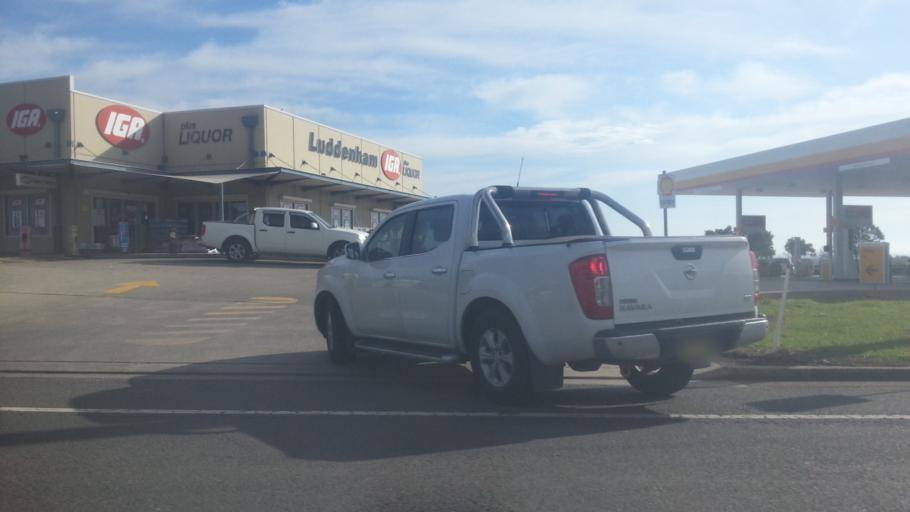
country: AU
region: New South Wales
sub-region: Liverpool
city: Luddenham
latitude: -33.8843
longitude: 150.6938
